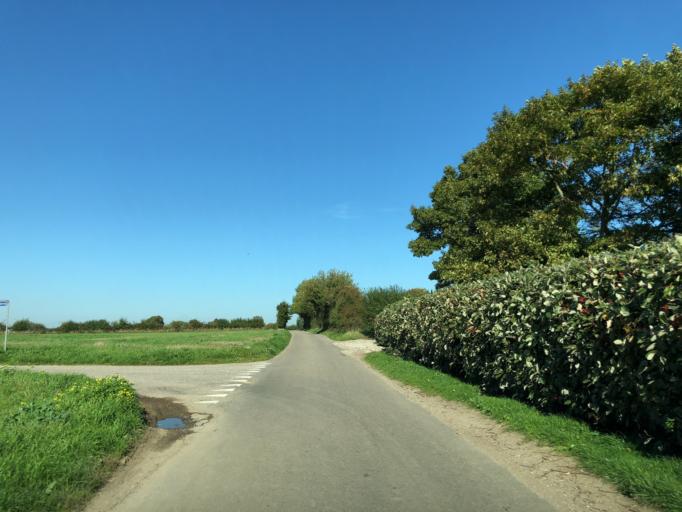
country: DK
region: South Denmark
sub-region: Sonderborg Kommune
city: Dybbol
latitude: 54.9606
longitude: 9.7330
